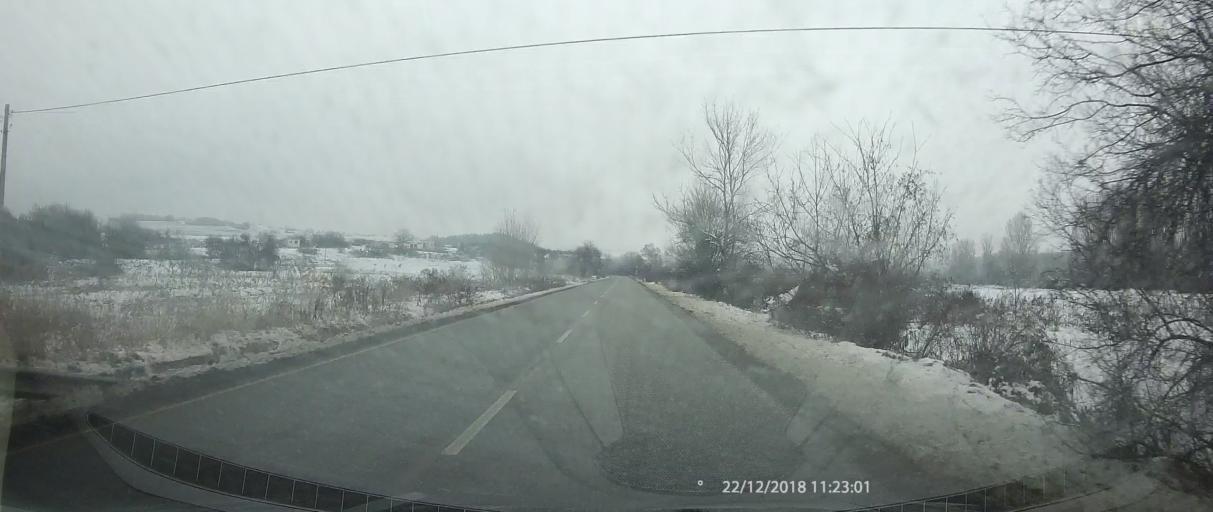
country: BG
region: Kyustendil
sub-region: Obshtina Boboshevo
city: Boboshevo
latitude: 42.2570
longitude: 22.8682
